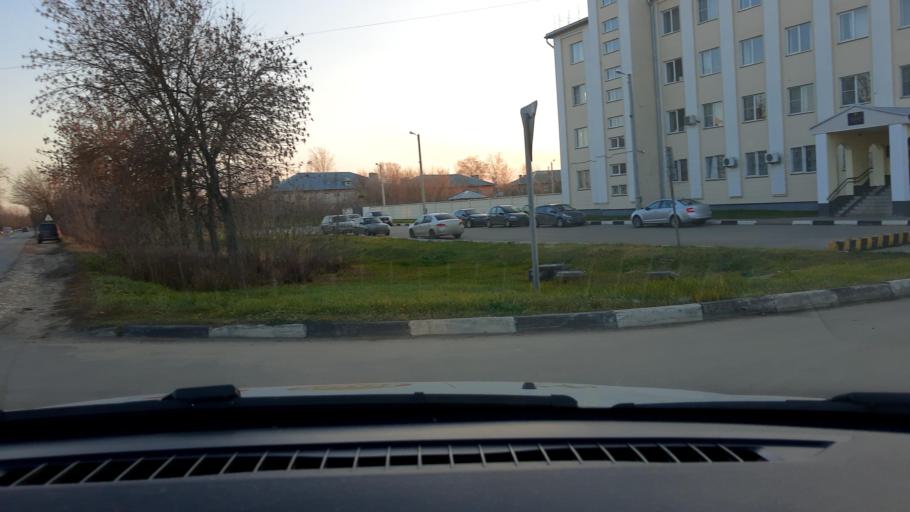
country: RU
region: Nizjnij Novgorod
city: Volodarsk
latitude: 56.2382
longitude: 43.1853
